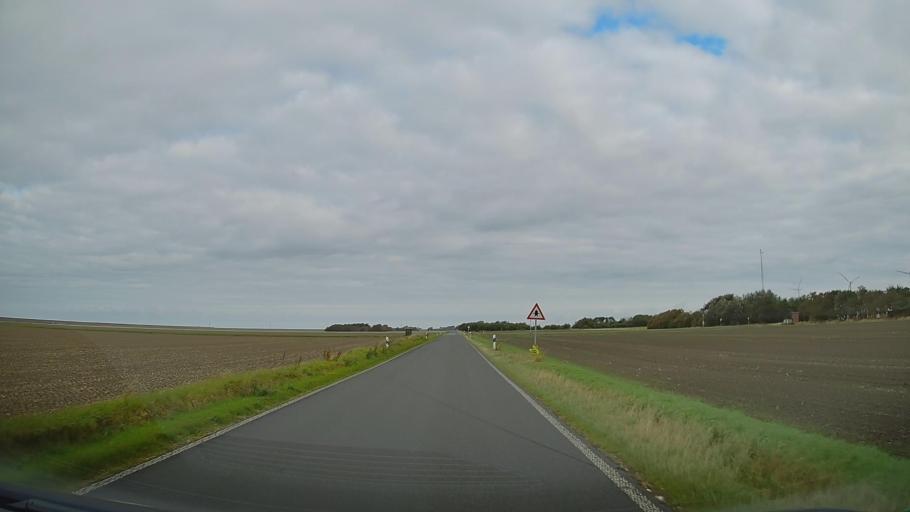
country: DE
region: Schleswig-Holstein
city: Friedrich-Wilhelm-Lubke-Koog
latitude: 54.8612
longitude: 8.6247
